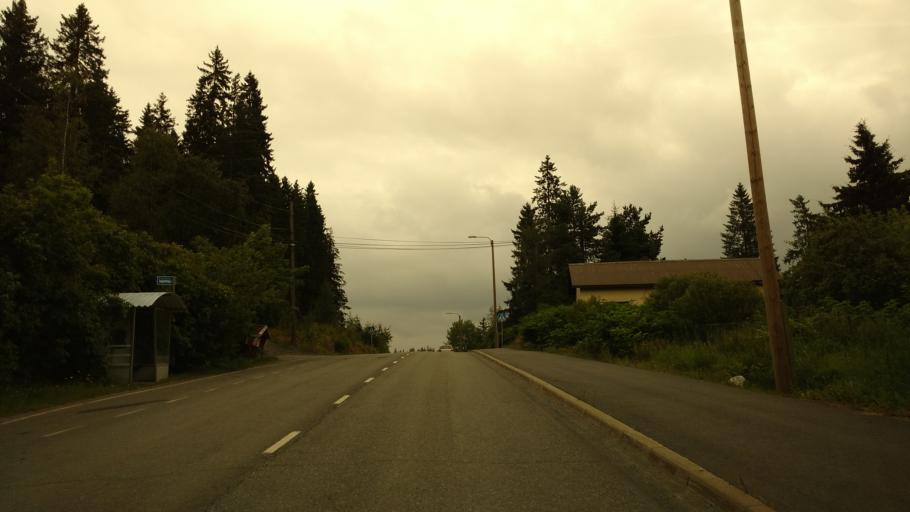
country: FI
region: Haeme
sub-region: Forssa
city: Ypaejae
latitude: 60.7987
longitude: 23.2793
